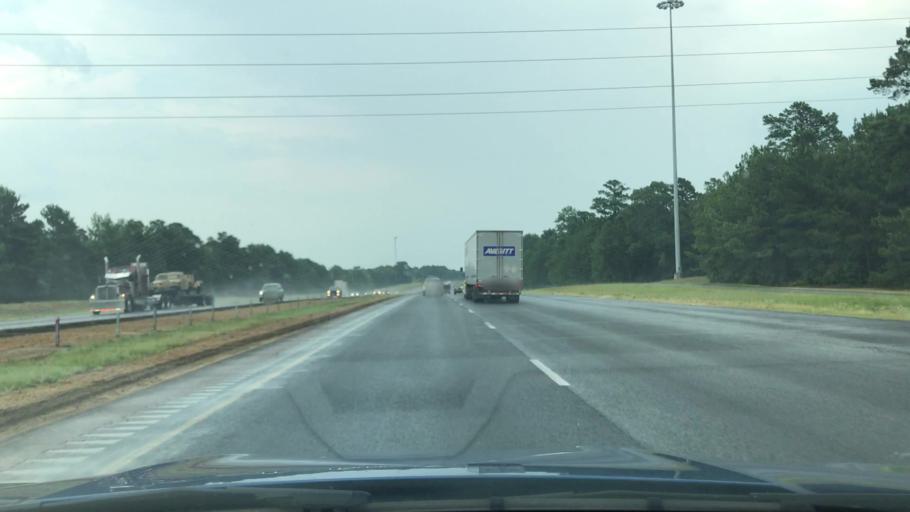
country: US
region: Texas
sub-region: Harrison County
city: Marshall
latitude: 32.4960
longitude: -94.2387
